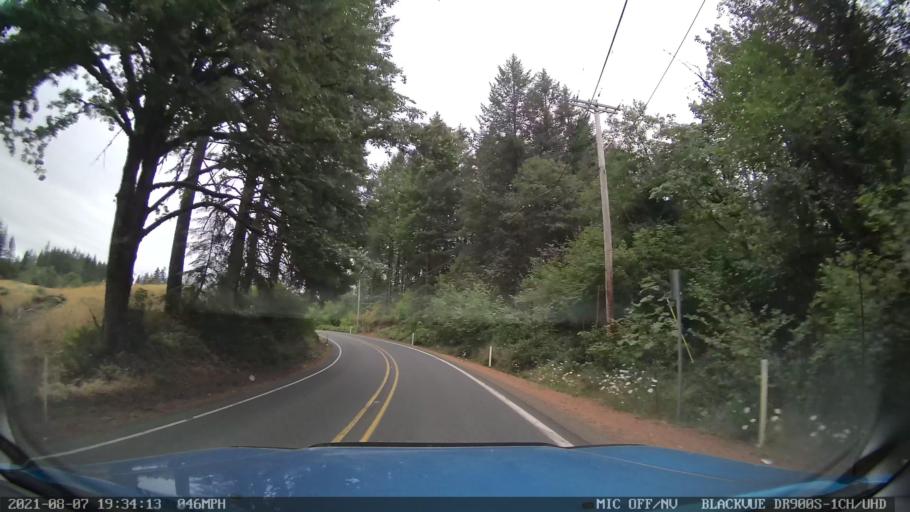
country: US
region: Oregon
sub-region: Linn County
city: Lyons
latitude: 44.9152
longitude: -122.6550
